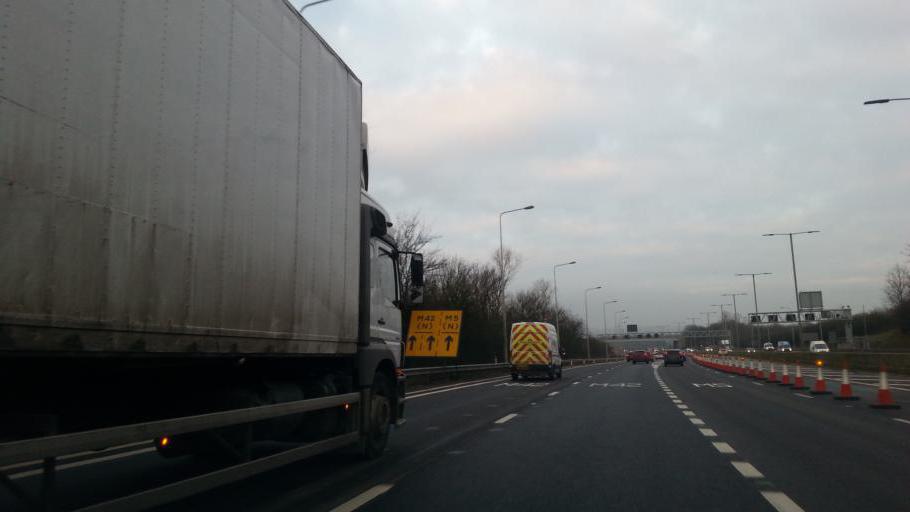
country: GB
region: England
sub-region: Worcestershire
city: Bromsgrove
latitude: 52.3457
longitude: -2.0792
